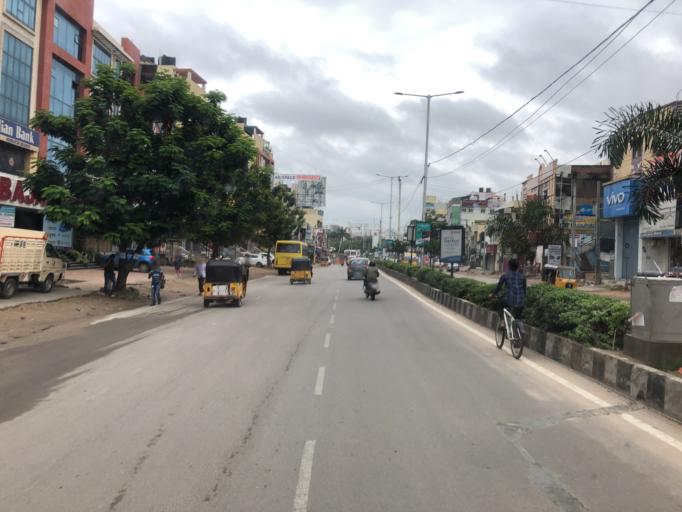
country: IN
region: Telangana
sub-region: Rangareddi
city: Kukatpalli
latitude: 17.4636
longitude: 78.3673
